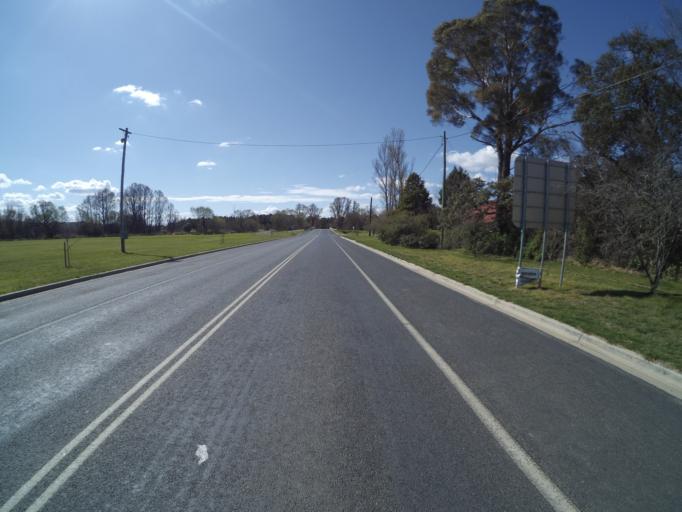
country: AU
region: New South Wales
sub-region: Palerang
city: Bungendore
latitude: -35.2526
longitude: 149.4386
